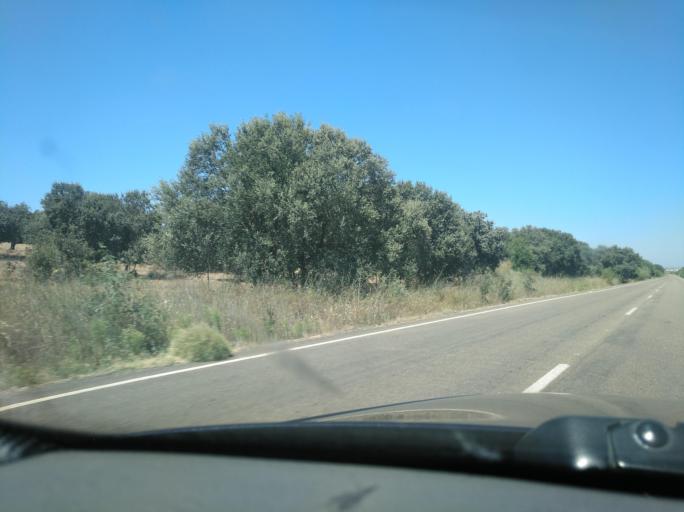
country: ES
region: Extremadura
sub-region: Provincia de Badajoz
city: Olivenza
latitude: 38.7162
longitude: -7.1967
